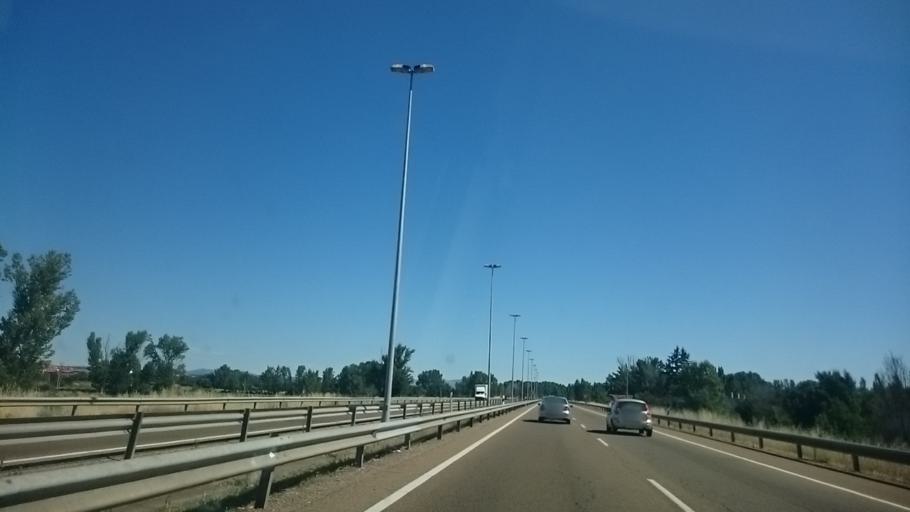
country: ES
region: Castille and Leon
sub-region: Provincia de Leon
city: Leon
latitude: 42.5918
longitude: -5.5532
